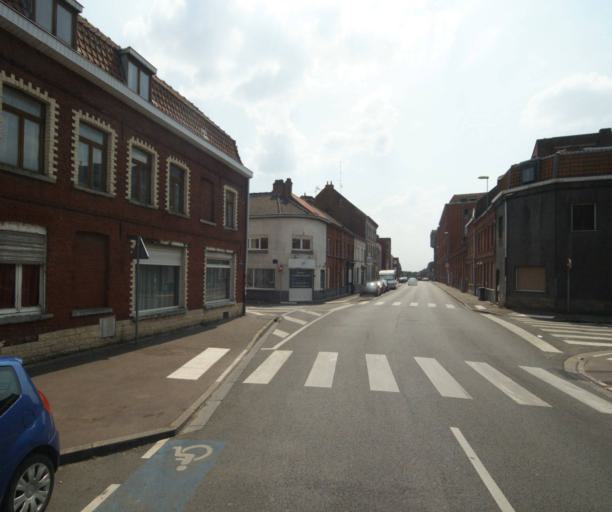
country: FR
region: Nord-Pas-de-Calais
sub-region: Departement du Nord
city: Tourcoing
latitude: 50.7222
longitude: 3.1444
